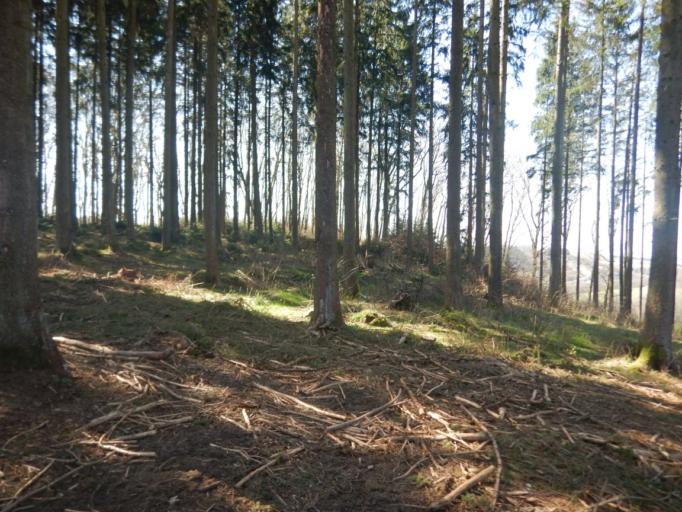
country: LU
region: Diekirch
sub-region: Canton de Clervaux
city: Troisvierges
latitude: 50.0994
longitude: 6.0258
